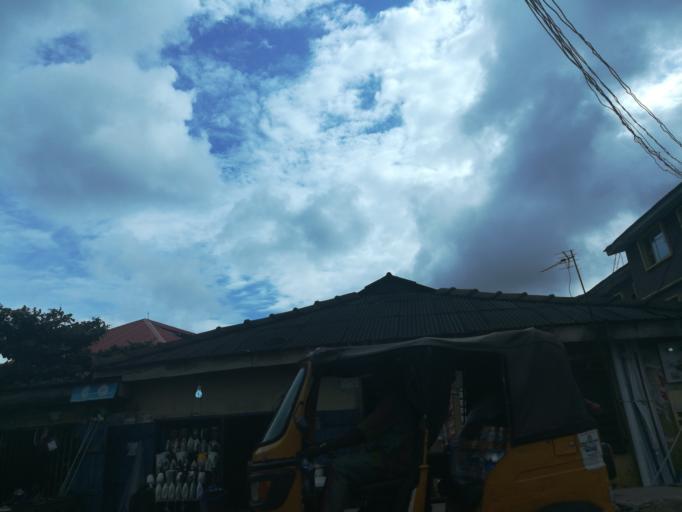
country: NG
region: Lagos
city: Agege
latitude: 6.6173
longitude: 3.3352
